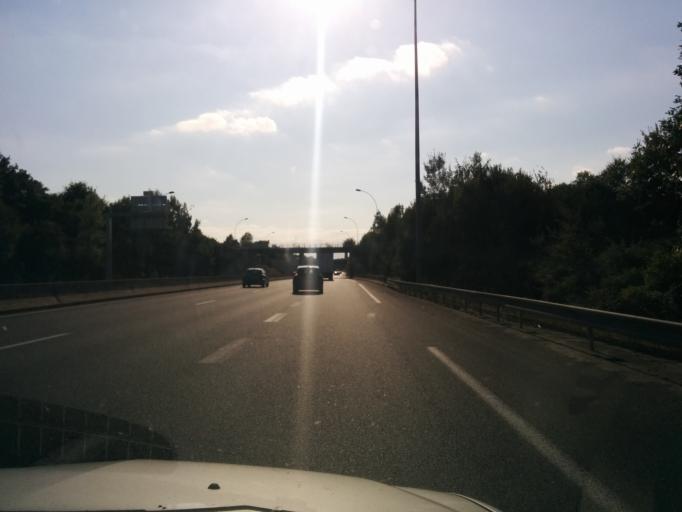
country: FR
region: Pays de la Loire
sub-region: Departement de la Loire-Atlantique
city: Carquefou
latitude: 47.2915
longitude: -1.4824
